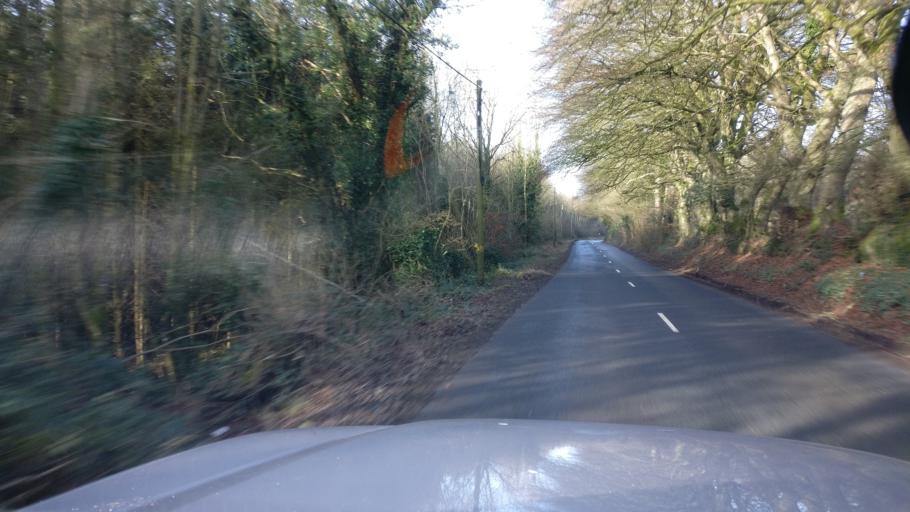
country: IE
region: Leinster
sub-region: Laois
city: Stradbally
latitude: 52.9421
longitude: -7.1995
